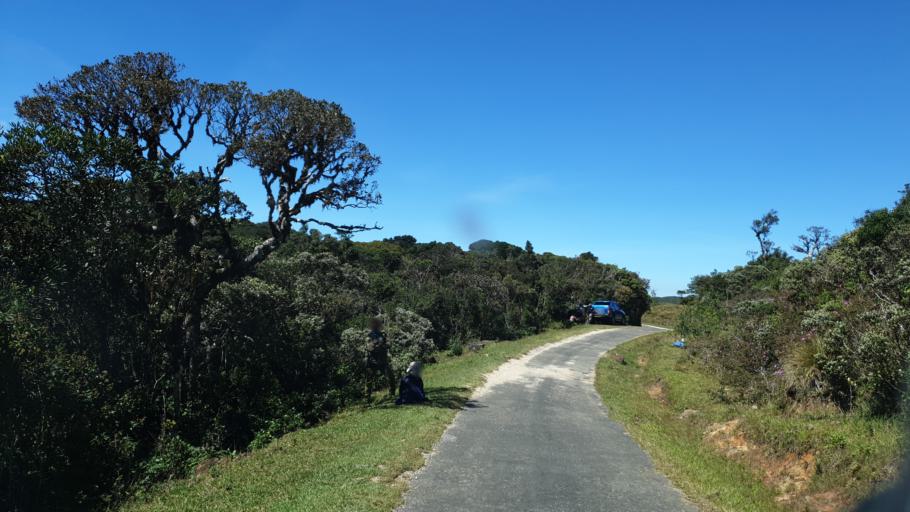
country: LK
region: Uva
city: Haputale
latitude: 6.8076
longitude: 80.8375
